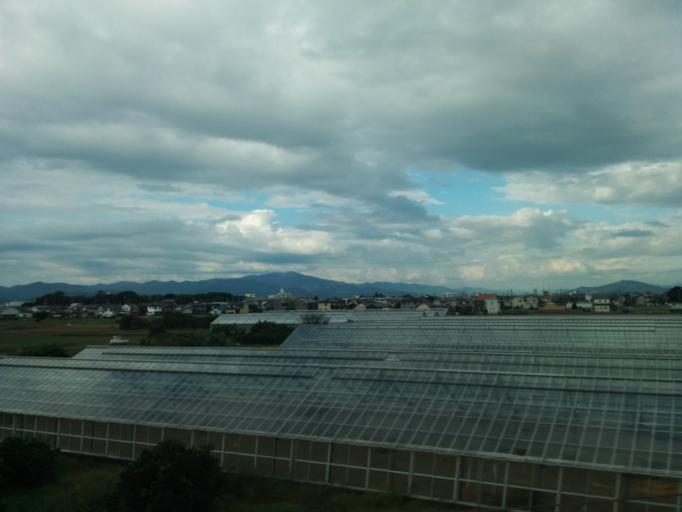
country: JP
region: Aichi
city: Kozakai-cho
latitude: 34.7913
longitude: 137.3453
